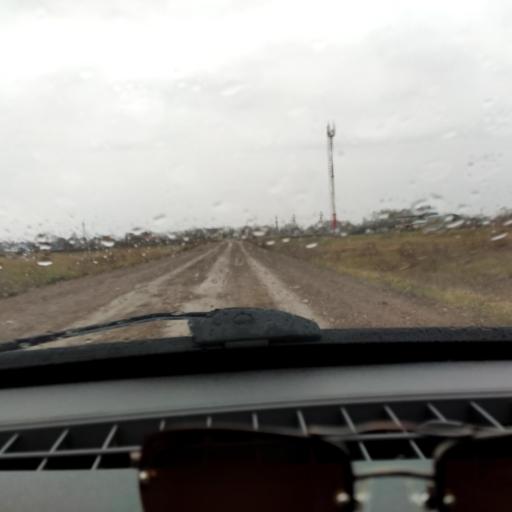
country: RU
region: Bashkortostan
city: Kabakovo
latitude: 54.5647
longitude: 56.0459
